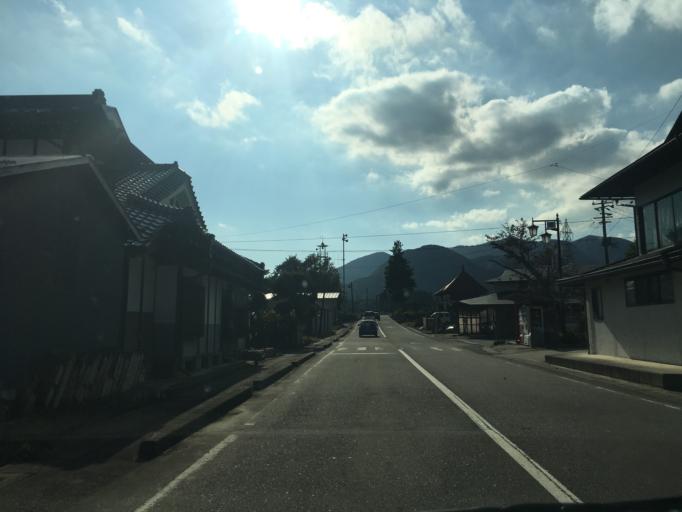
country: JP
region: Fukushima
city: Sukagawa
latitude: 37.2771
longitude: 140.1656
